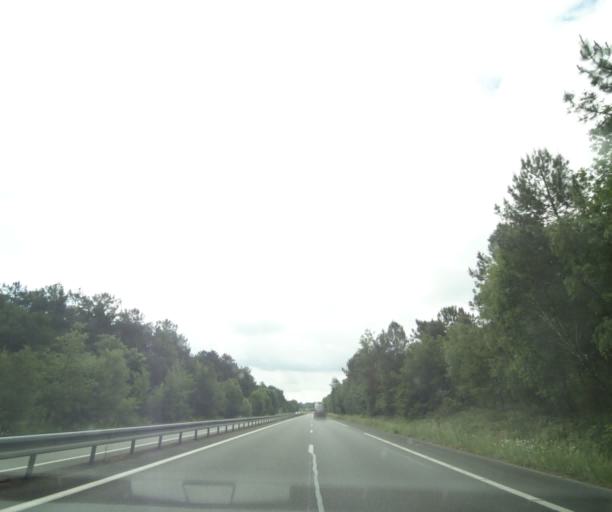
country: FR
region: Pays de la Loire
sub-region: Departement de Maine-et-Loire
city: Baune
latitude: 47.5173
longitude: -0.3028
